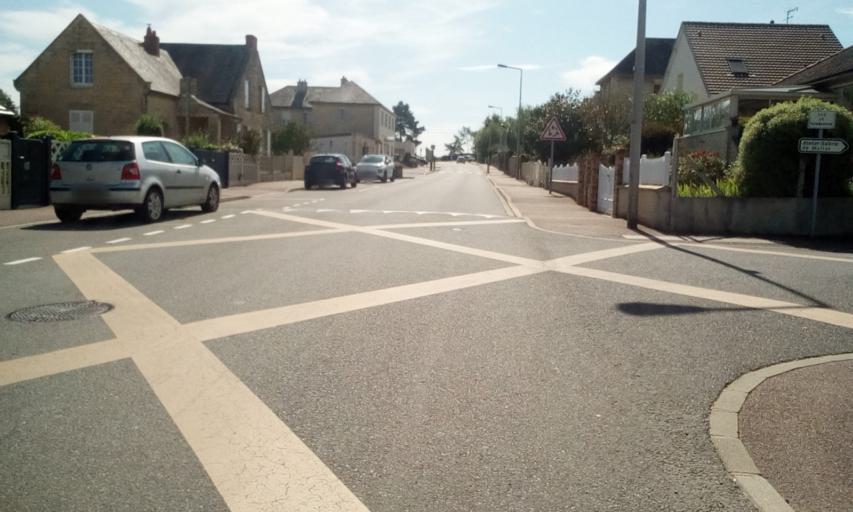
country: FR
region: Lower Normandy
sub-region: Departement du Calvados
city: Eterville
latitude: 49.1292
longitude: -0.4220
